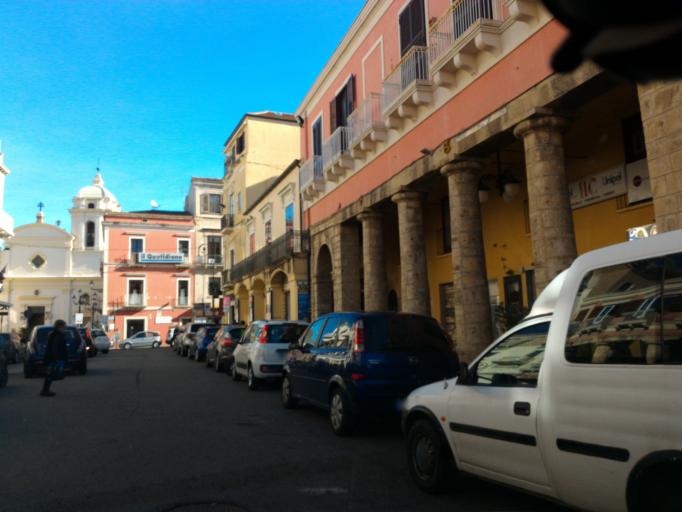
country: IT
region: Calabria
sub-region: Provincia di Crotone
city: Crotone
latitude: 39.0809
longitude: 17.1277
